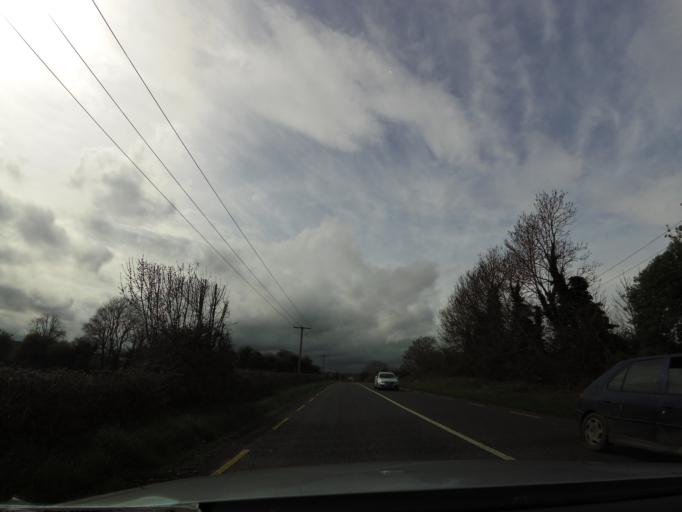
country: IE
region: Leinster
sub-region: Kilkenny
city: Ballyragget
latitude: 52.7258
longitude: -7.3710
